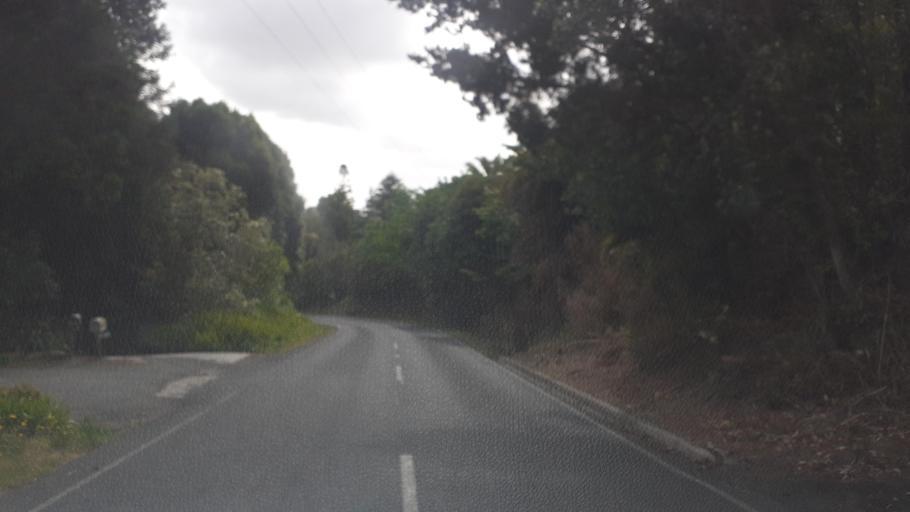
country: NZ
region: Northland
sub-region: Far North District
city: Kerikeri
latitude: -35.2172
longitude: 173.9818
